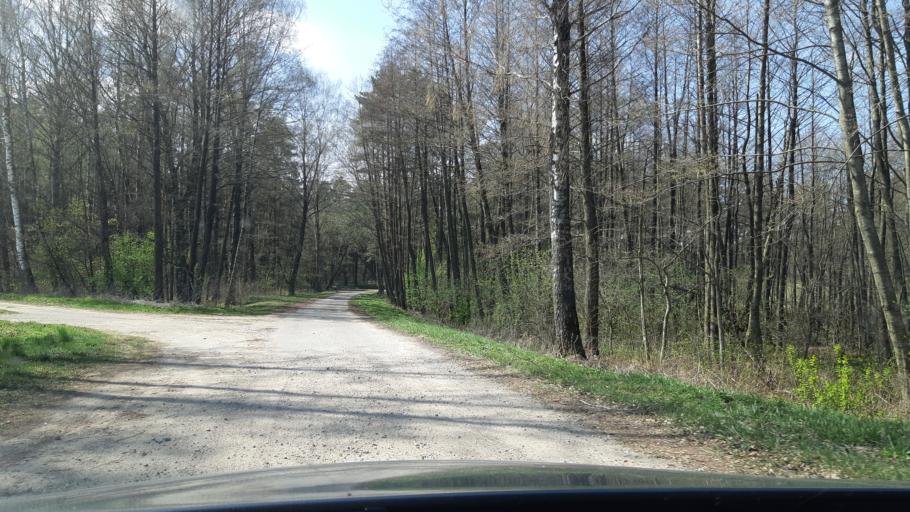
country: LT
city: Virbalis
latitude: 54.5700
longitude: 22.9072
